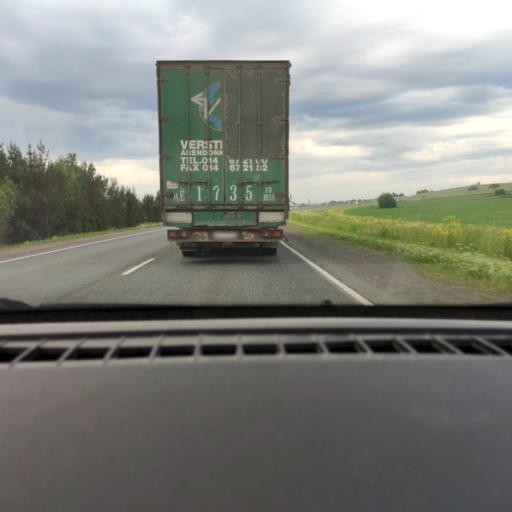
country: RU
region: Perm
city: Chastyye
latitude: 57.3872
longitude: 54.4374
